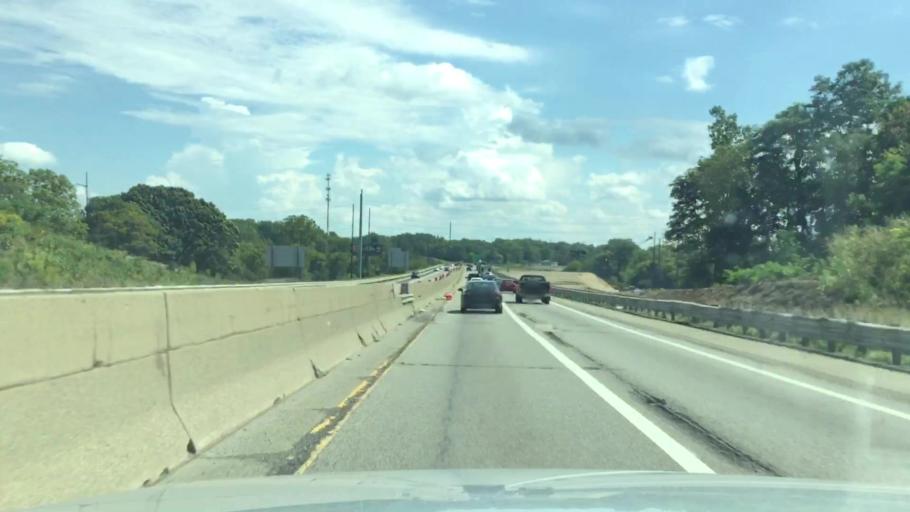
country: US
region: Michigan
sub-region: Jackson County
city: Jackson
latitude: 42.2721
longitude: -84.4148
